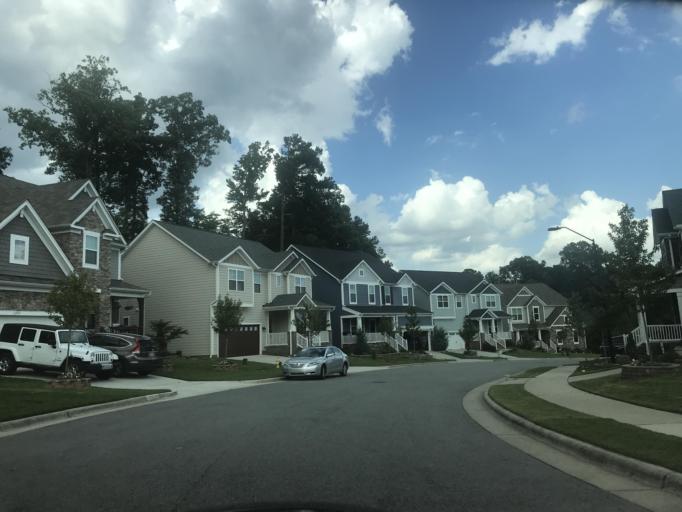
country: US
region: North Carolina
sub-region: Wake County
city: Knightdale
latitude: 35.8403
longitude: -78.5544
